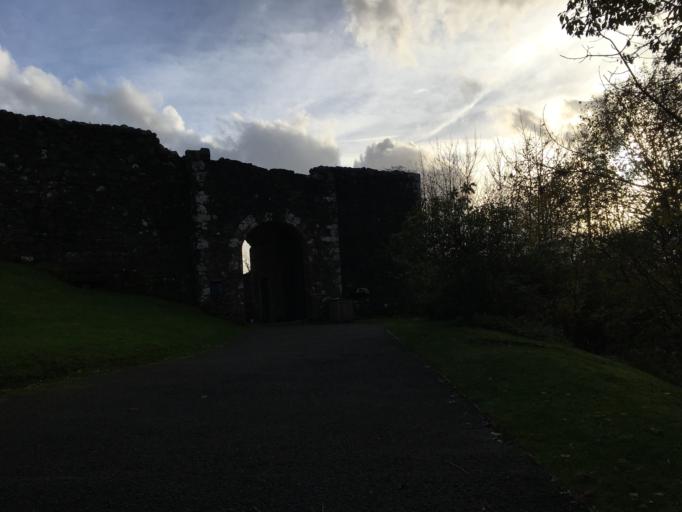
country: GB
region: Scotland
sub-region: Clackmannanshire
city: Dollar
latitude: 56.1752
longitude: -3.6749
